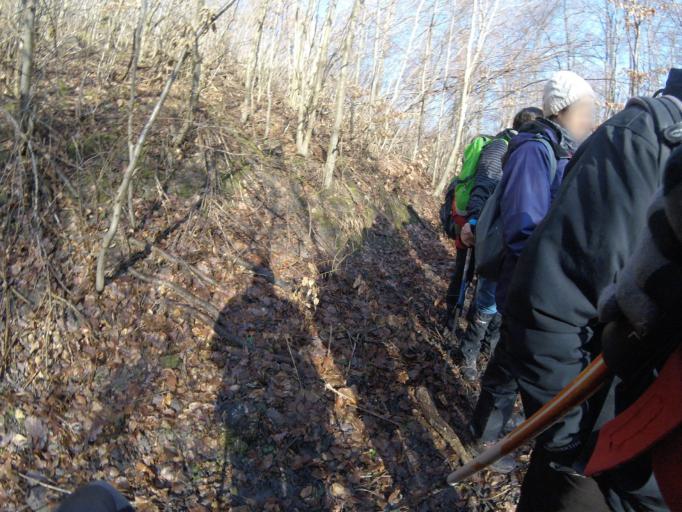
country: HU
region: Komarom-Esztergom
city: Pilismarot
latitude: 47.7421
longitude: 18.8830
